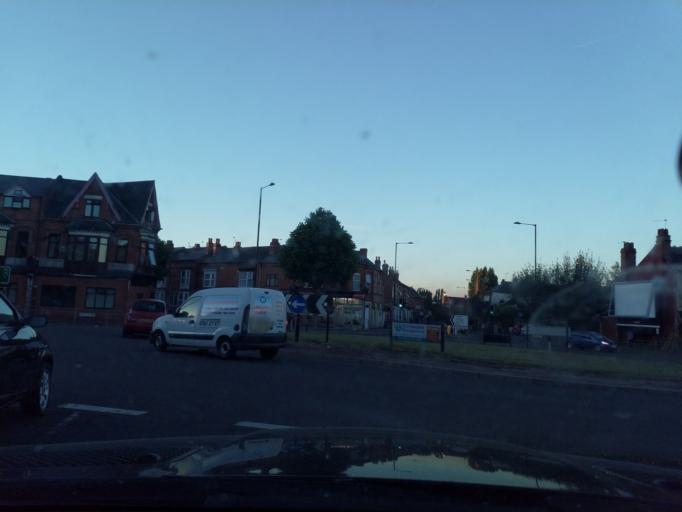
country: GB
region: England
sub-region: City and Borough of Birmingham
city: Birmingham
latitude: 52.4558
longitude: -1.8631
